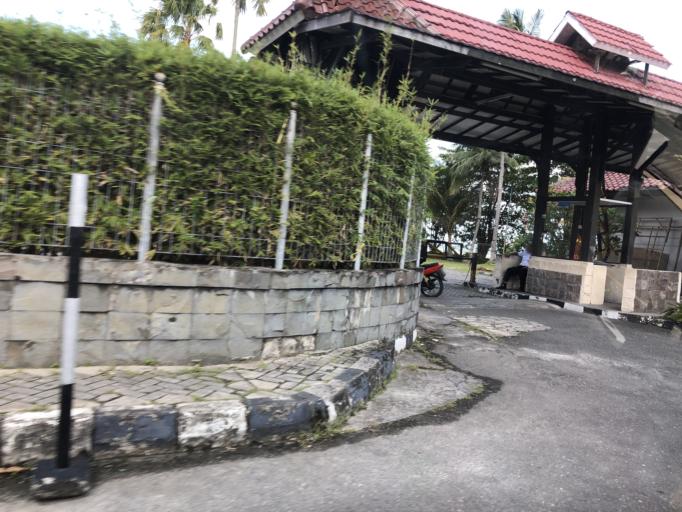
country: ID
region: East Kalimantan
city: Balikpapan
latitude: -1.2742
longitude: 116.8517
